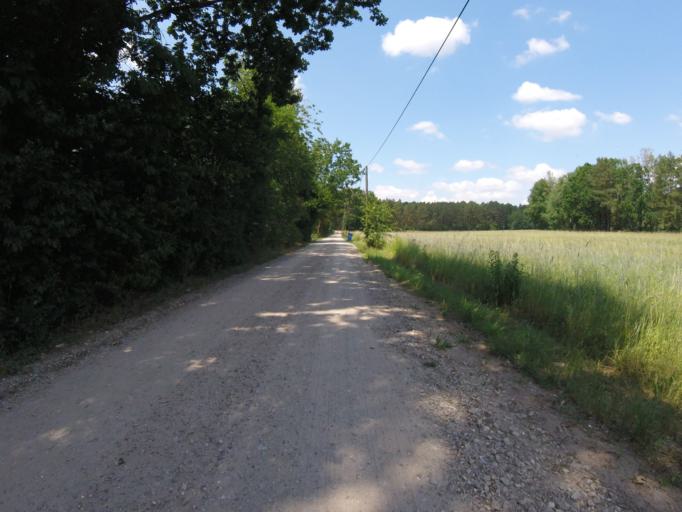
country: DE
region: Brandenburg
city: Bestensee
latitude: 52.2467
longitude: 13.6915
